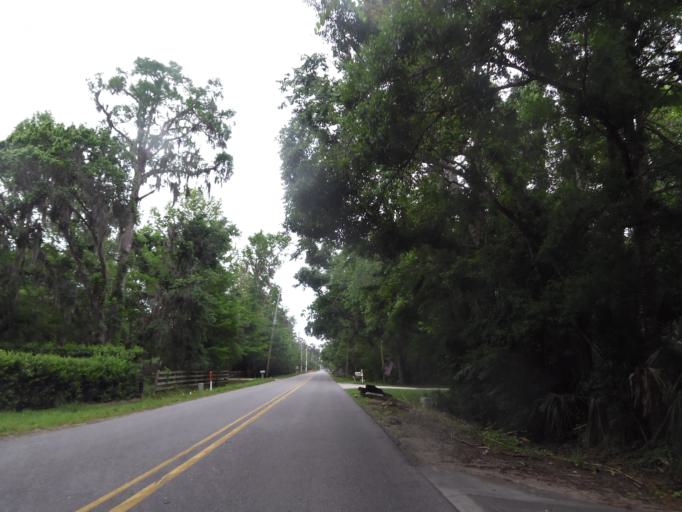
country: US
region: Florida
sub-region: Saint Johns County
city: Palm Valley
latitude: 30.1864
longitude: -81.4027
